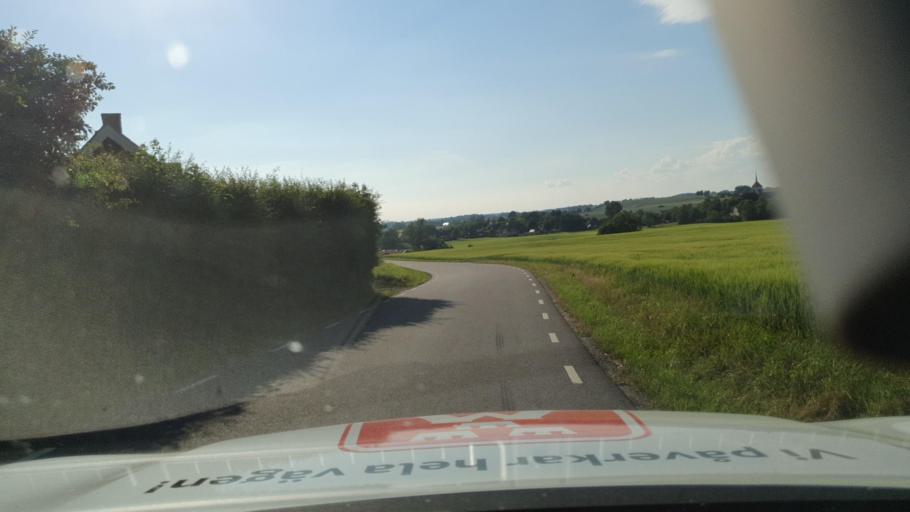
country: SE
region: Skane
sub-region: Skurups Kommun
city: Rydsgard
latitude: 55.5065
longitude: 13.5580
